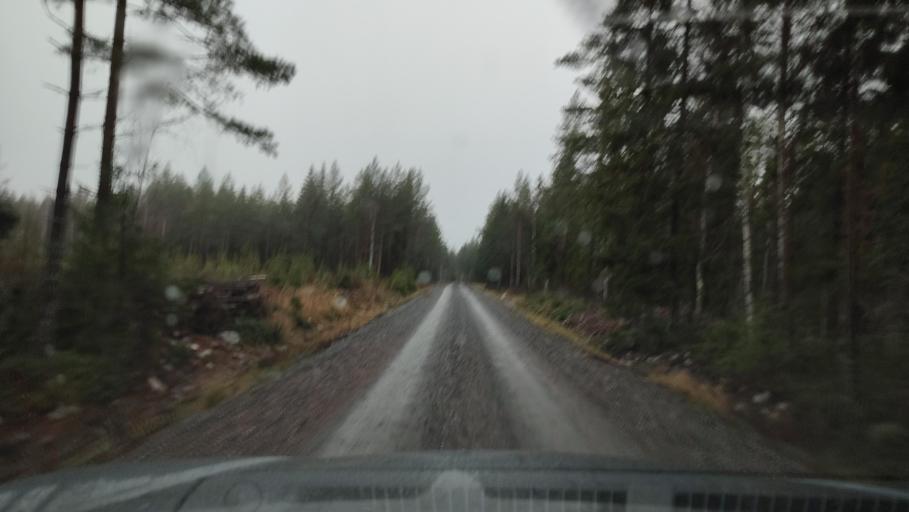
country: FI
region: Southern Ostrobothnia
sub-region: Suupohja
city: Karijoki
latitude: 62.1776
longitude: 21.6971
